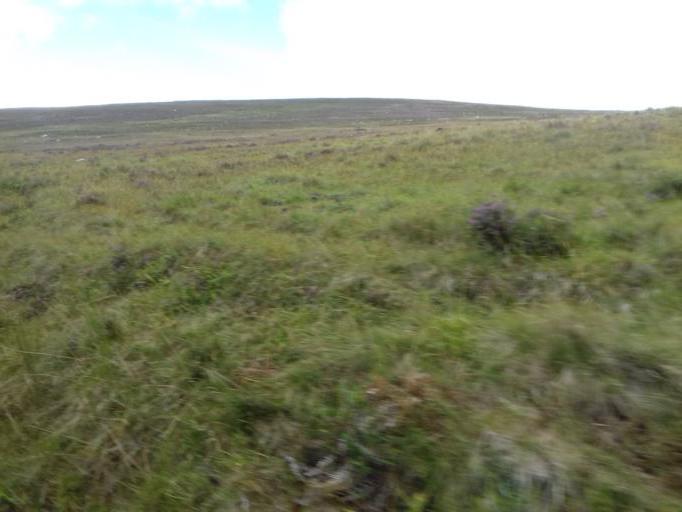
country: IE
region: Leinster
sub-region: Loch Garman
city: Bunclody
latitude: 52.6354
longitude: -6.8012
